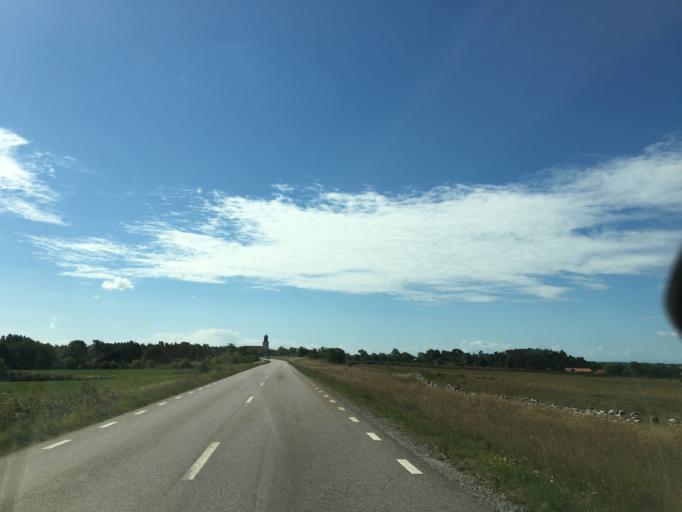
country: SE
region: Kalmar
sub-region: Morbylanga Kommun
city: Moerbylanga
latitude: 56.5478
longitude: 16.4426
